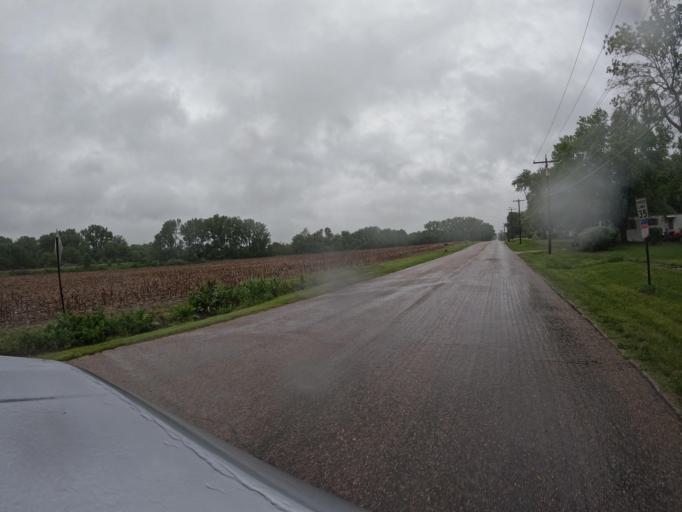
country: US
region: Nebraska
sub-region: Gage County
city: Wymore
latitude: 40.1224
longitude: -96.6536
